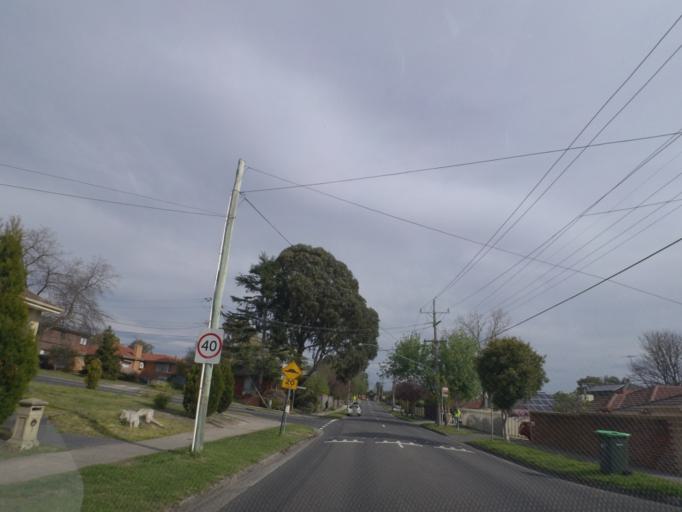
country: AU
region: Victoria
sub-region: Whitehorse
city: Vermont
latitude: -37.8412
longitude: 145.2001
